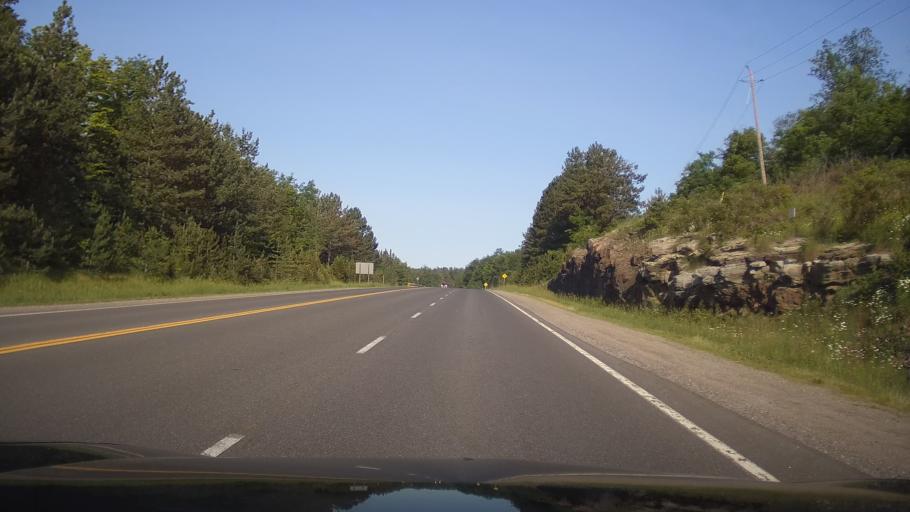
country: CA
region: Ontario
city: Quinte West
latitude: 44.5019
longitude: -77.5273
